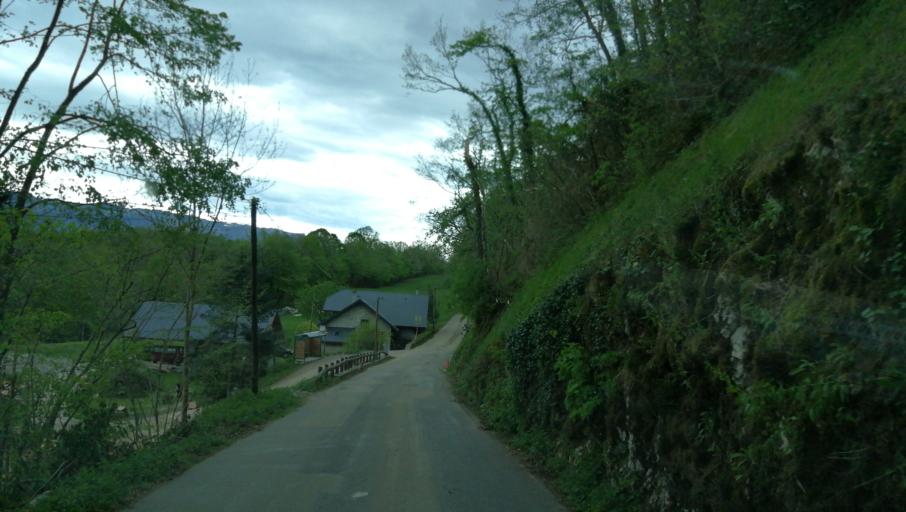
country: FR
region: Rhone-Alpes
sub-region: Departement de la Savoie
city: Brison-Saint-Innocent
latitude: 45.7283
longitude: 5.8465
